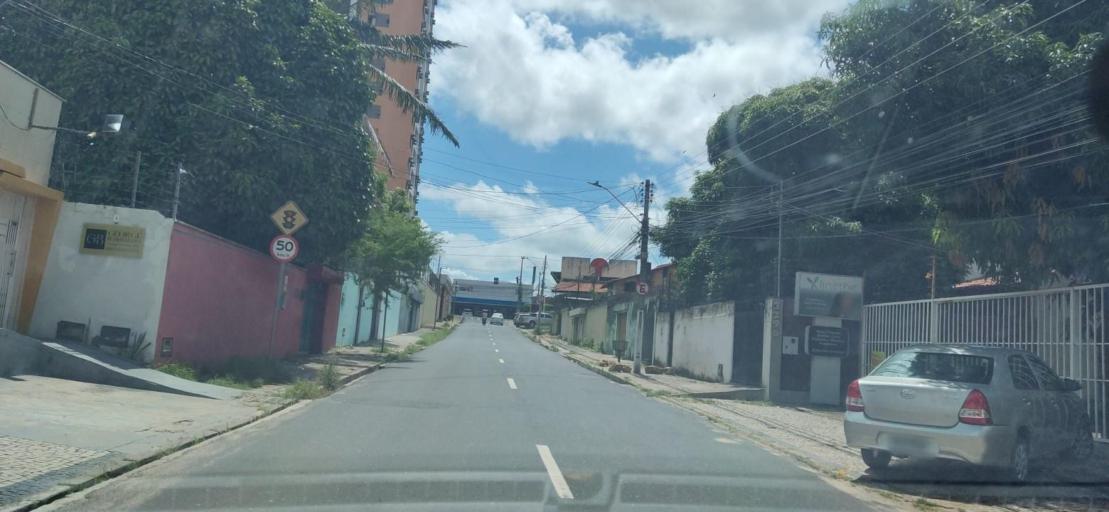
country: BR
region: Piaui
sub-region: Teresina
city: Teresina
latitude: -5.0660
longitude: -42.7715
